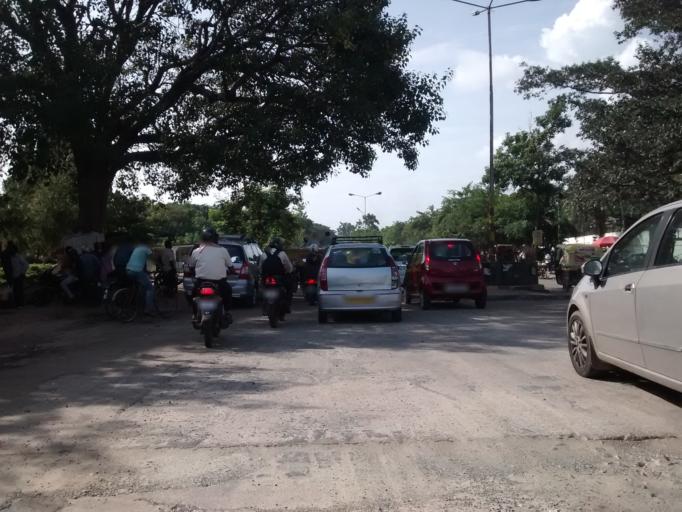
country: IN
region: Karnataka
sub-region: Bangalore Urban
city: Bangalore
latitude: 12.9834
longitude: 77.6494
